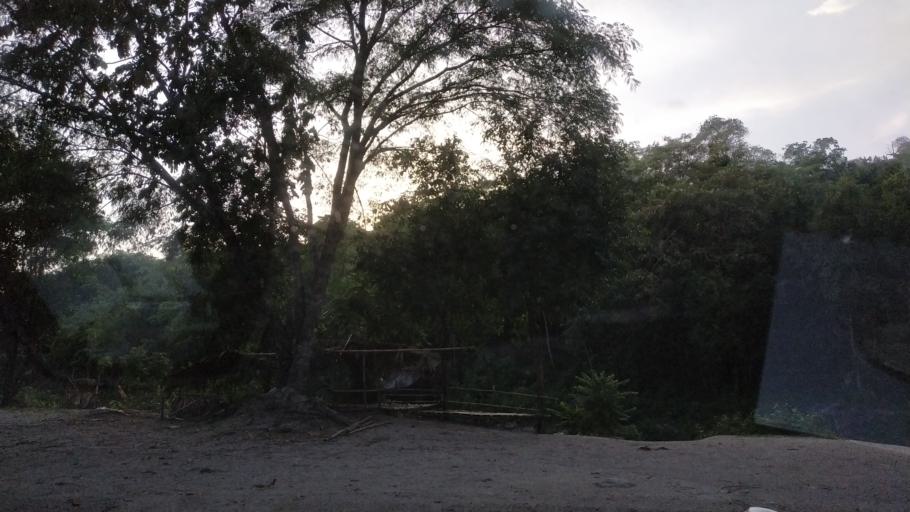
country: MM
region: Mon
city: Kyaikto
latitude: 17.4416
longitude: 97.0427
